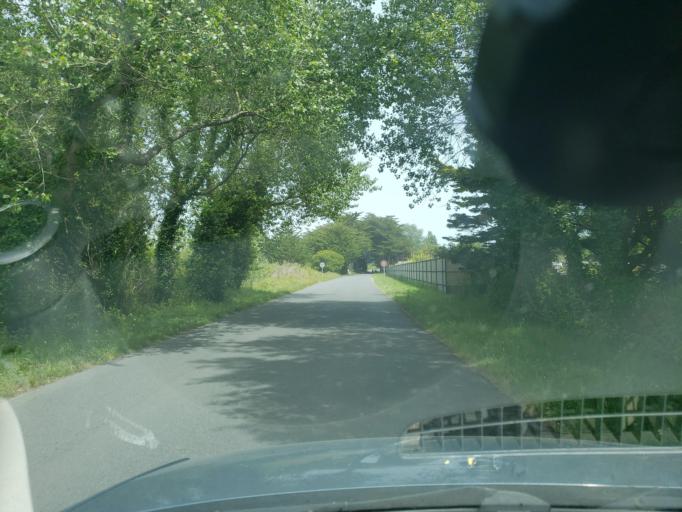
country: FR
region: Brittany
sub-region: Departement du Finistere
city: Guilvinec
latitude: 47.8038
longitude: -4.3166
